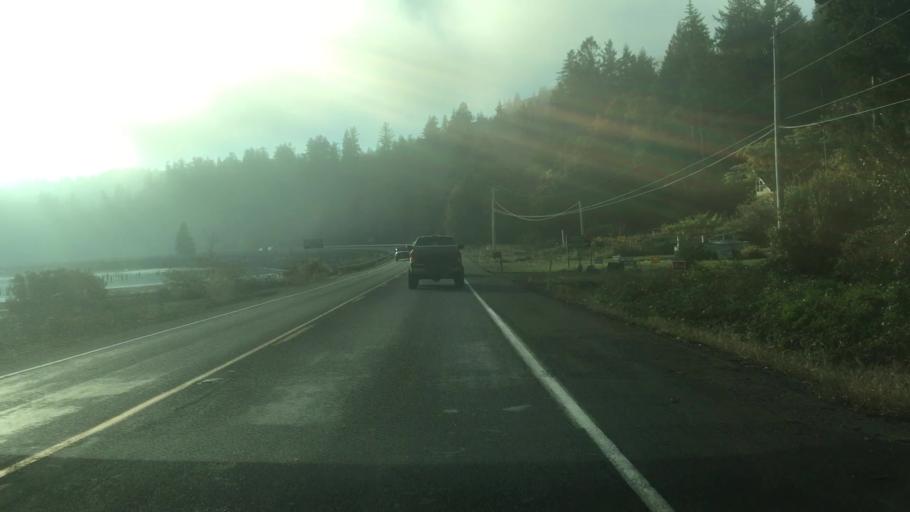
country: US
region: Oregon
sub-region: Clatsop County
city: Astoria
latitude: 46.2702
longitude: -123.8289
